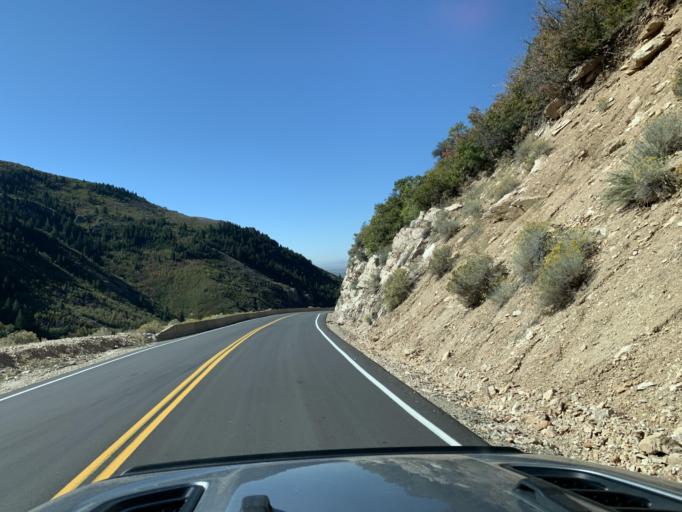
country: US
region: Utah
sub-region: Weber County
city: North Ogden
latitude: 41.3132
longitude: -111.9129
